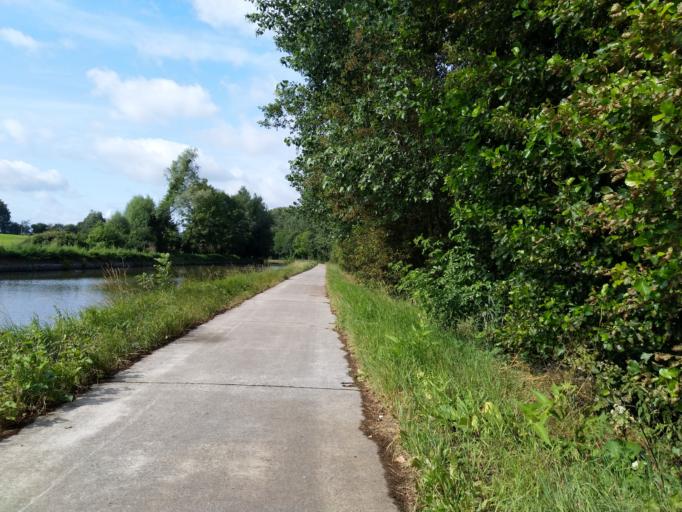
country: BE
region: Wallonia
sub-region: Province du Hainaut
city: Chievres
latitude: 50.5781
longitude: 3.7730
